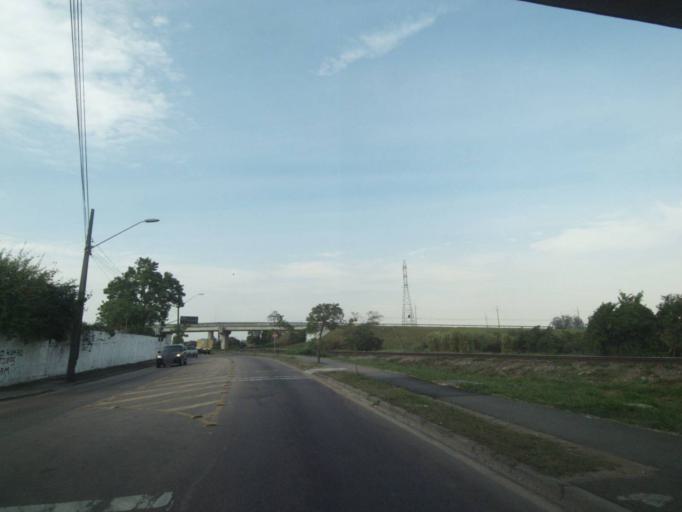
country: BR
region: Parana
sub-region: Sao Jose Dos Pinhais
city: Sao Jose dos Pinhais
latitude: -25.5025
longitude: -49.2097
